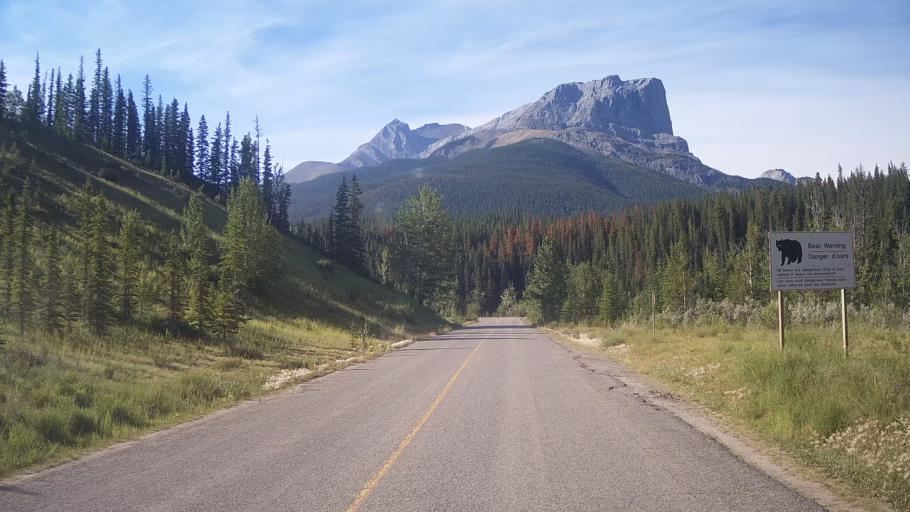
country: CA
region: Alberta
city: Jasper Park Lodge
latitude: 53.2014
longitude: -117.9227
